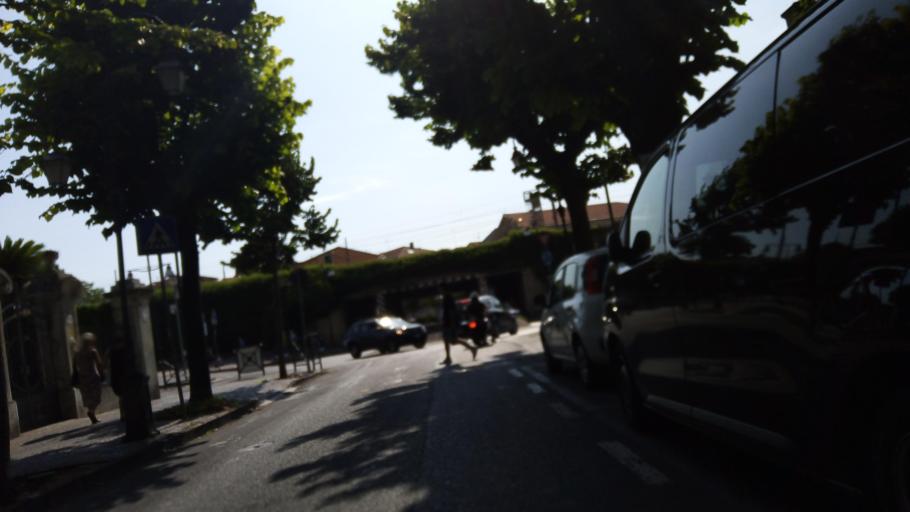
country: IT
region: Liguria
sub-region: Provincia di Savona
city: Albenga
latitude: 44.0468
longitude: 8.2194
